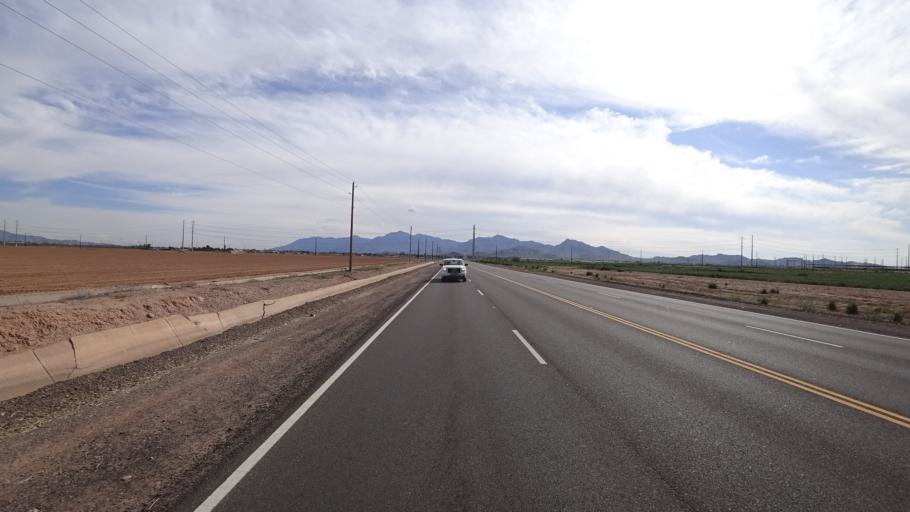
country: US
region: Arizona
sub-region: Maricopa County
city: Avondale
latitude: 33.4166
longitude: -112.3062
